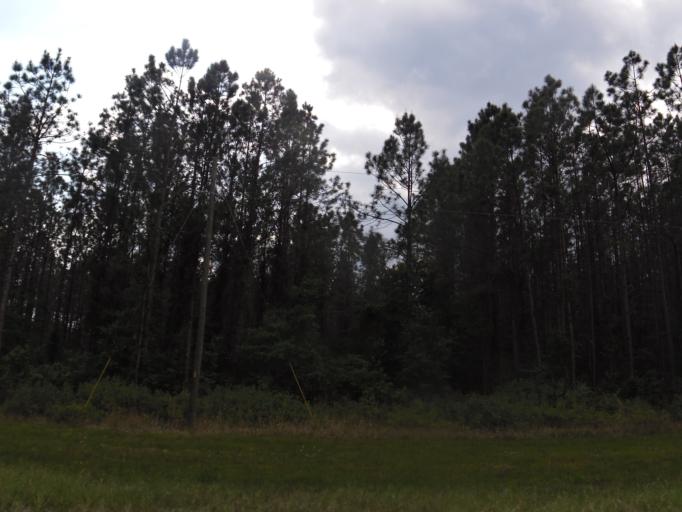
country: US
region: Georgia
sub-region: Charlton County
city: Folkston
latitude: 30.8676
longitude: -82.0136
